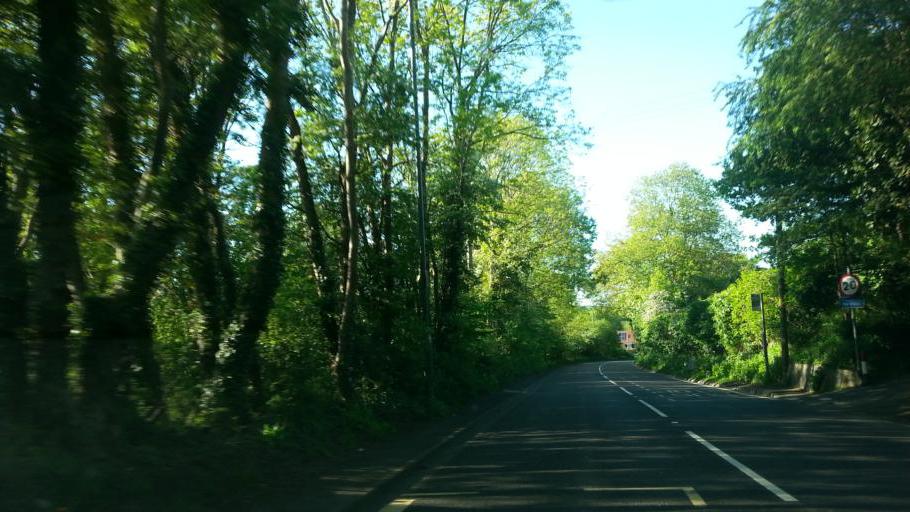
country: GB
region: England
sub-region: Bath and North East Somerset
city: Publow
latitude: 51.3670
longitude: -2.5481
